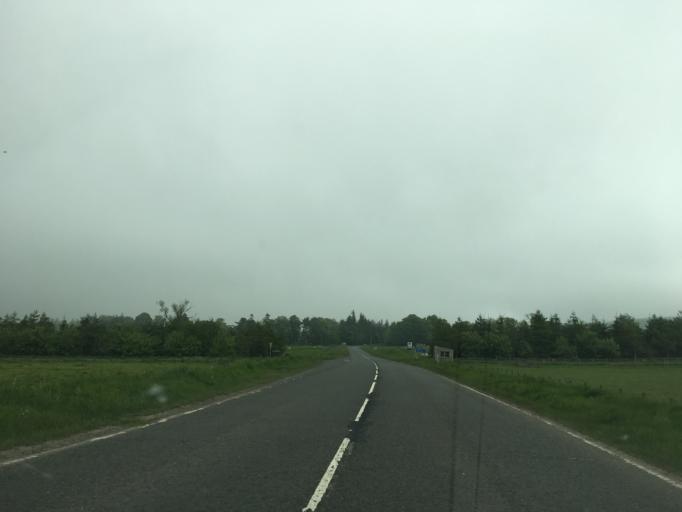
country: GB
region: Scotland
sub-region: The Scottish Borders
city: West Linton
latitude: 55.7277
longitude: -3.3201
